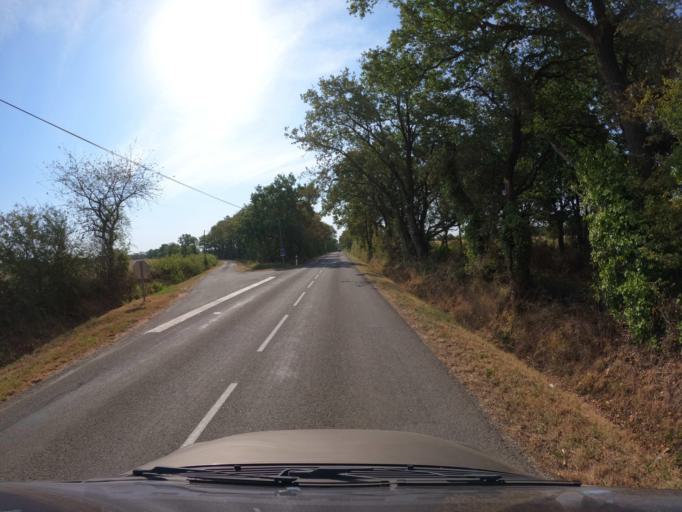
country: FR
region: Pays de la Loire
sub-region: Departement de la Vendee
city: Saint-Christophe-du-Ligneron
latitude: 46.8117
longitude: -1.8094
